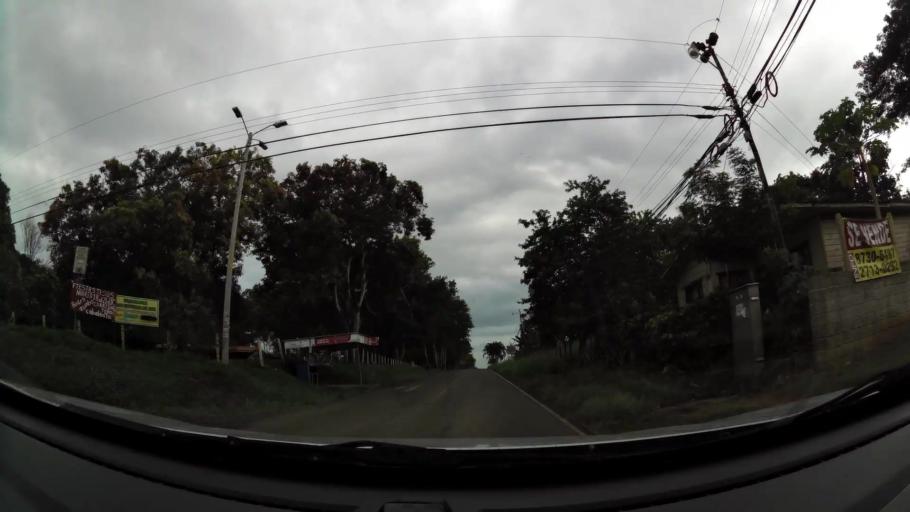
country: CR
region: Puntarenas
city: Esparza
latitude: 9.9755
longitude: -84.6188
